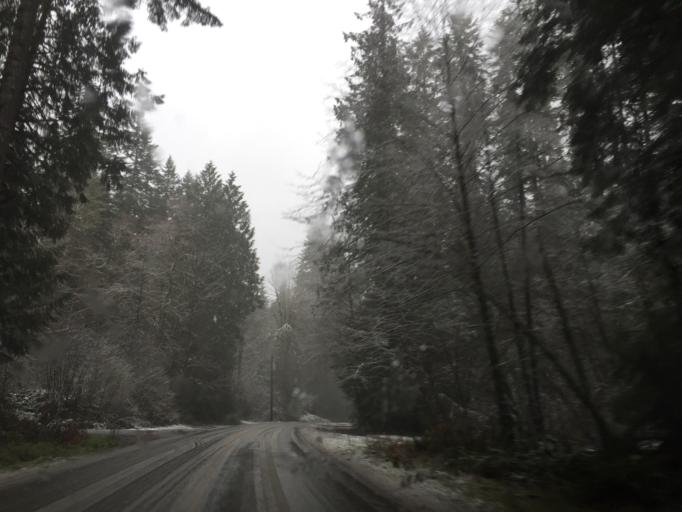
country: US
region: Washington
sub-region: Thurston County
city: Rochester
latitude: 46.9534
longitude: -123.0756
